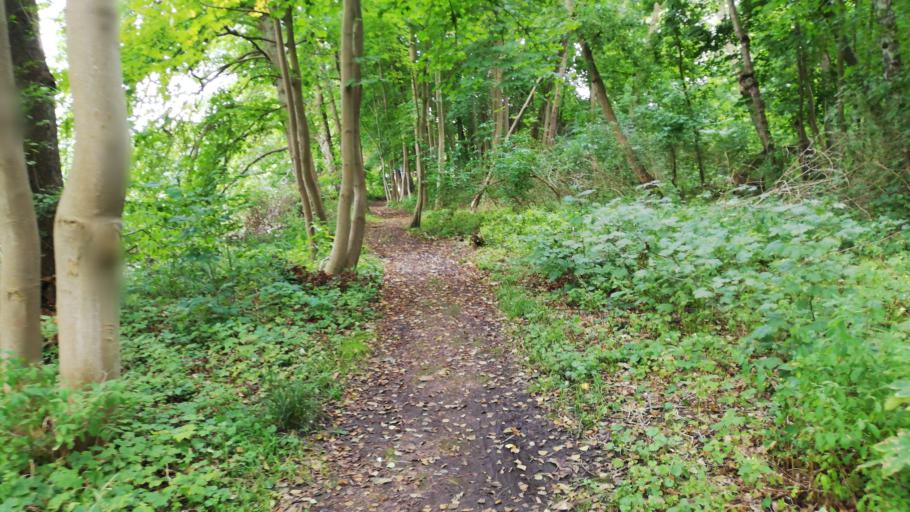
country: DE
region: Brandenburg
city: Furstenberg
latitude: 53.1832
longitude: 13.1595
